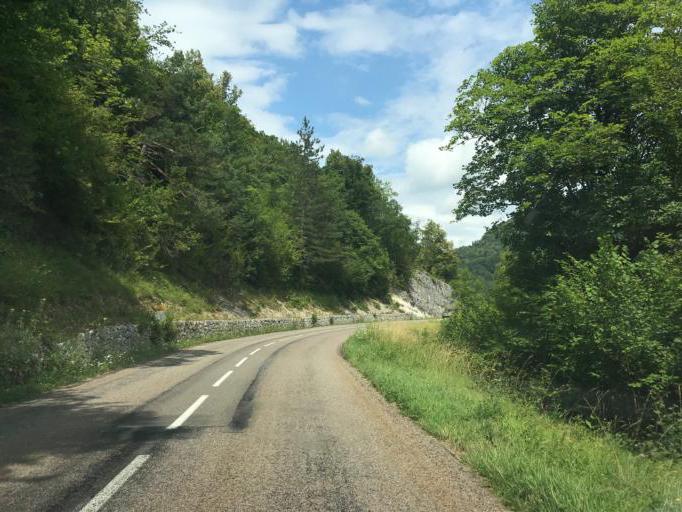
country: FR
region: Franche-Comte
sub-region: Departement du Jura
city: Saint-Claude
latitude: 46.4106
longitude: 5.8646
